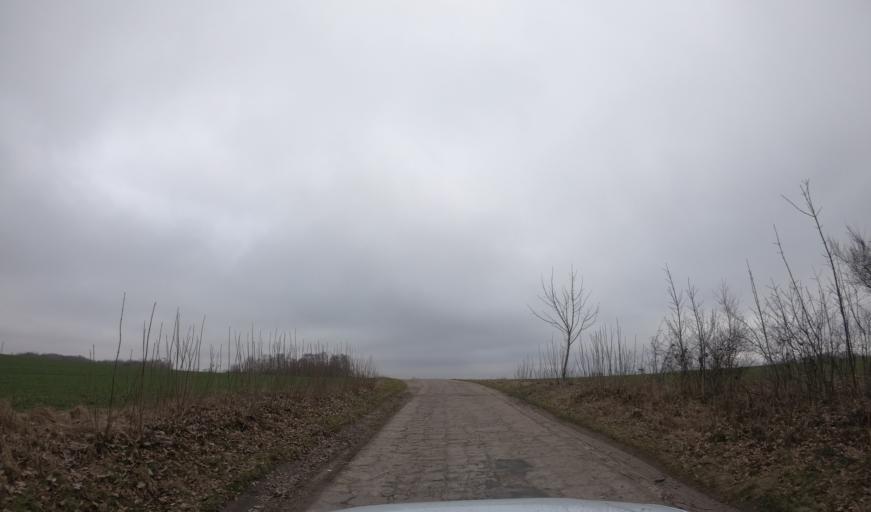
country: PL
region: West Pomeranian Voivodeship
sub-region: Powiat gryficki
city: Ploty
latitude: 53.8557
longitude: 15.2667
